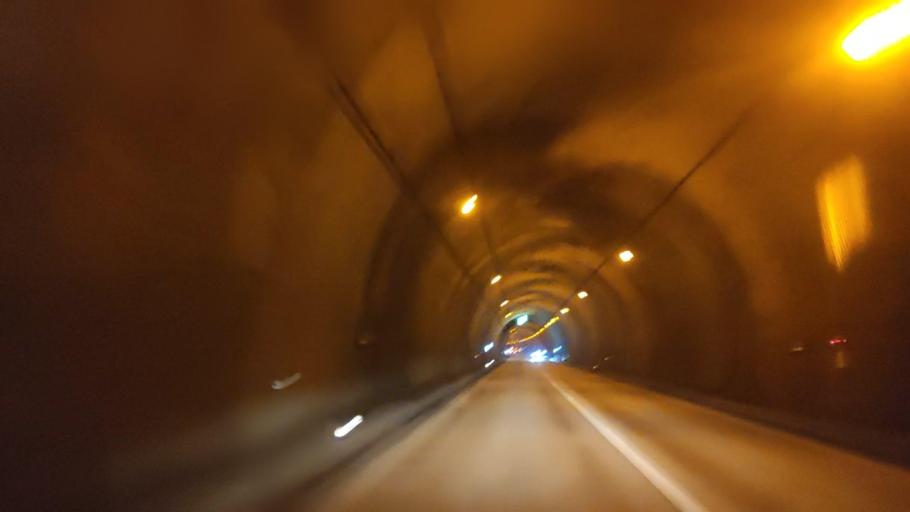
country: JP
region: Tottori
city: Kurayoshi
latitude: 35.3097
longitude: 133.7488
